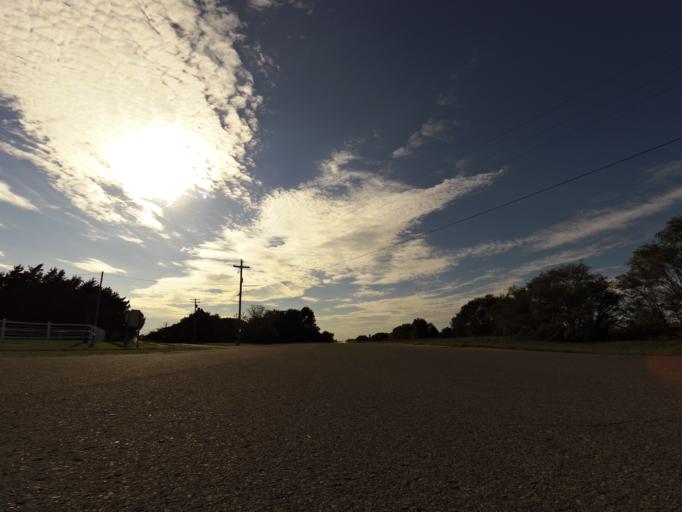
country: US
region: Kansas
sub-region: Reno County
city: Haven
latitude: 37.9410
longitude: -97.8726
